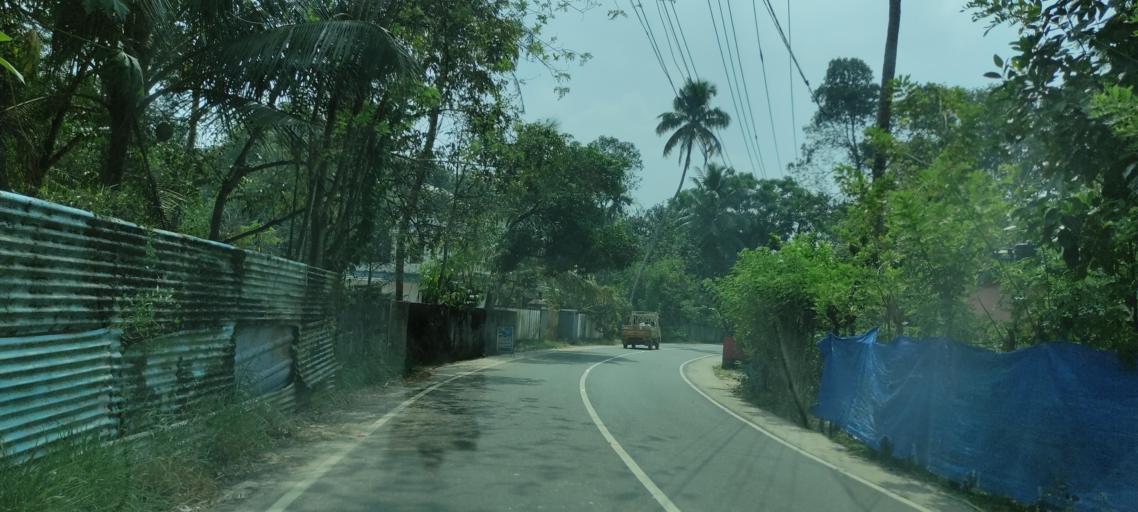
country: IN
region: Kerala
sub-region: Alappuzha
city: Shertallai
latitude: 9.5929
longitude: 76.3394
